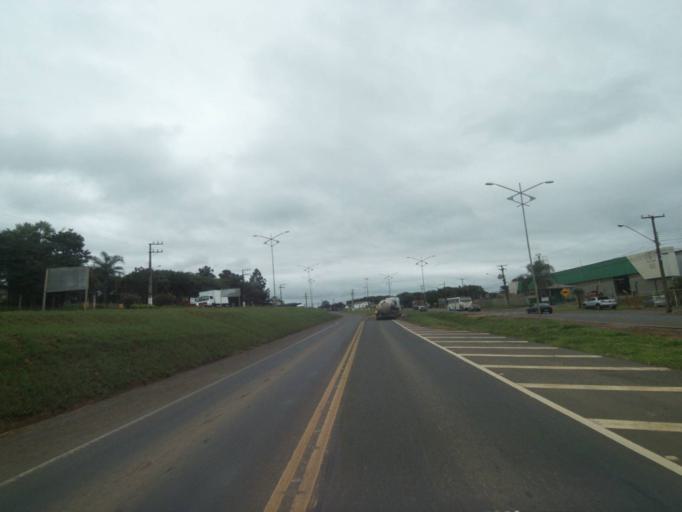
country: BR
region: Parana
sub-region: Telemaco Borba
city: Telemaco Borba
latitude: -24.3449
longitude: -50.6591
